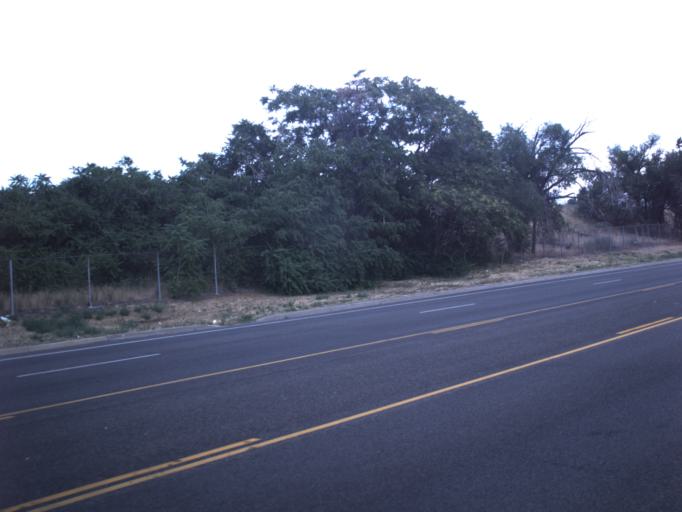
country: US
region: Utah
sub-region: Weber County
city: Roy
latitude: 41.1521
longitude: -112.0261
